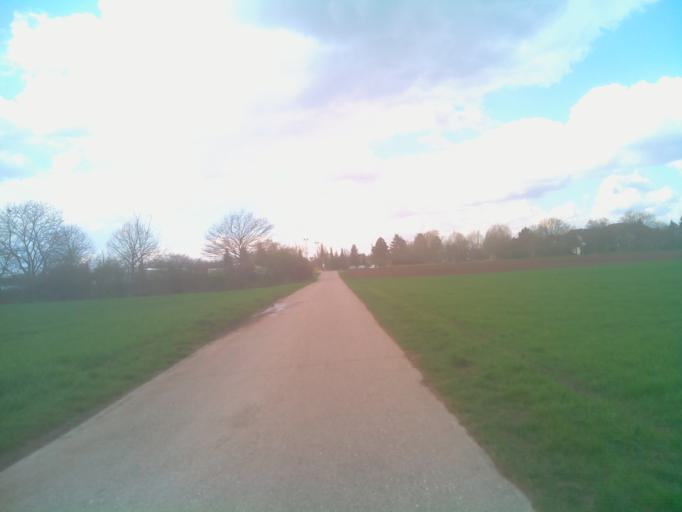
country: DE
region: Baden-Wuerttemberg
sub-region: Karlsruhe Region
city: Ladenburg
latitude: 49.4659
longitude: 8.6176
